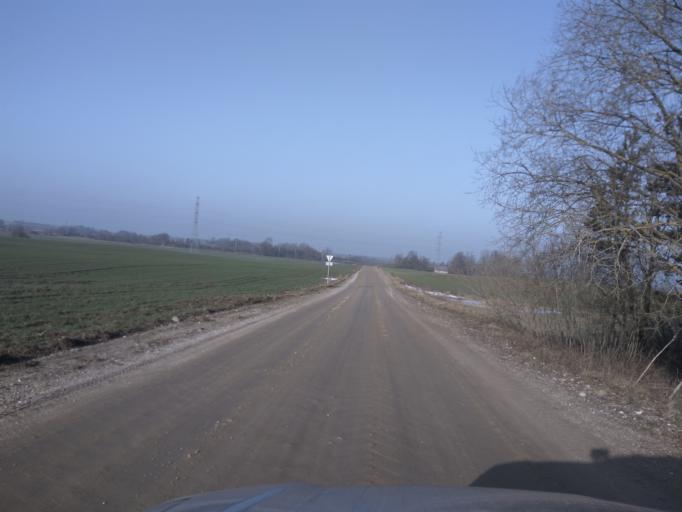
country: LV
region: Durbe
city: Liegi
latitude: 56.6624
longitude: 21.3487
